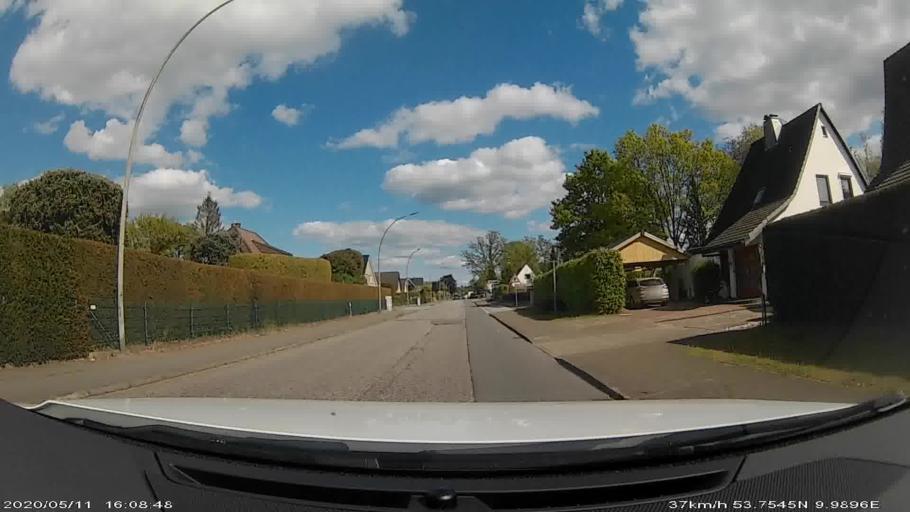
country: DE
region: Schleswig-Holstein
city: Henstedt-Ulzburg
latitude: 53.7531
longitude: 9.9981
